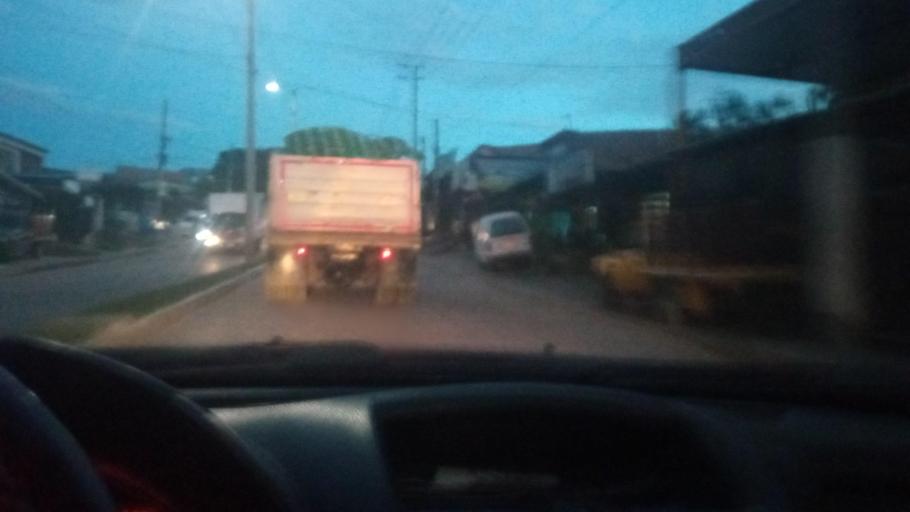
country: CO
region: Huila
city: Pitalito
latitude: 1.8588
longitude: -76.0480
